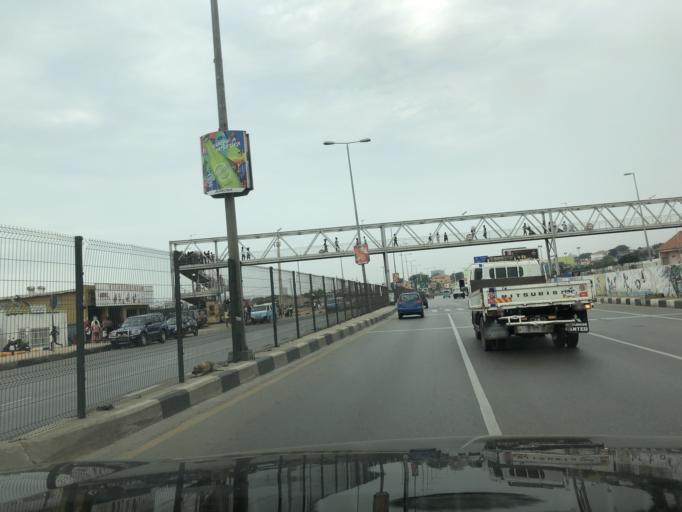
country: AO
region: Luanda
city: Luanda
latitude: -8.8532
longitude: 13.2200
